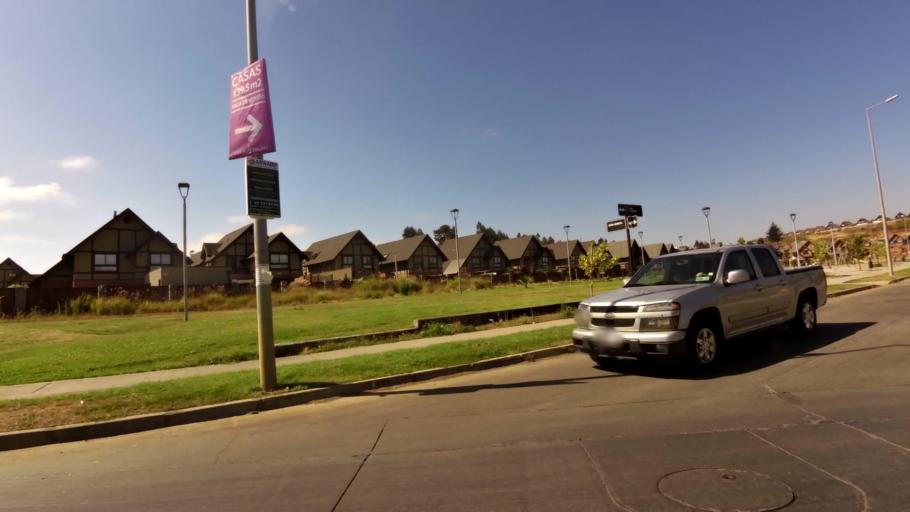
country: CL
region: Biobio
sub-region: Provincia de Concepcion
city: Concepcion
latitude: -36.7881
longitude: -73.0524
